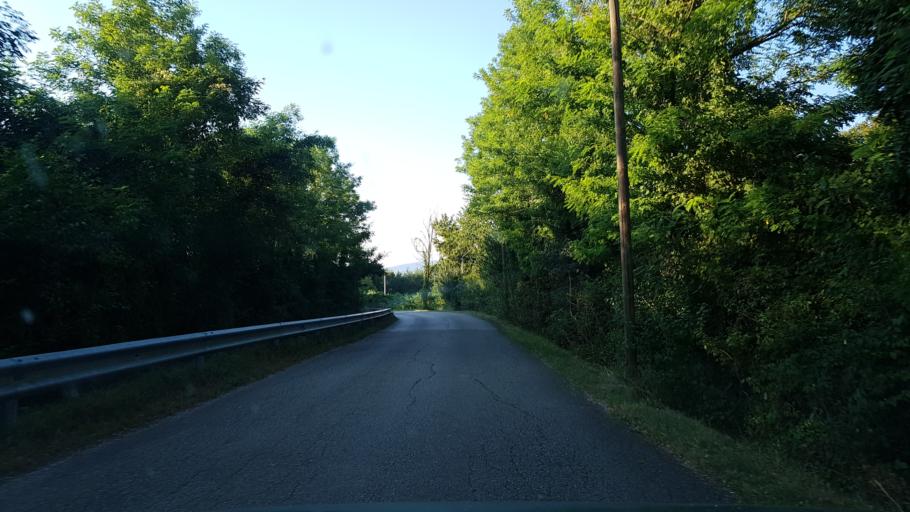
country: IT
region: Friuli Venezia Giulia
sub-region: Provincia di Gorizia
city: Capriva del Friuli
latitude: 45.9523
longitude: 13.5193
